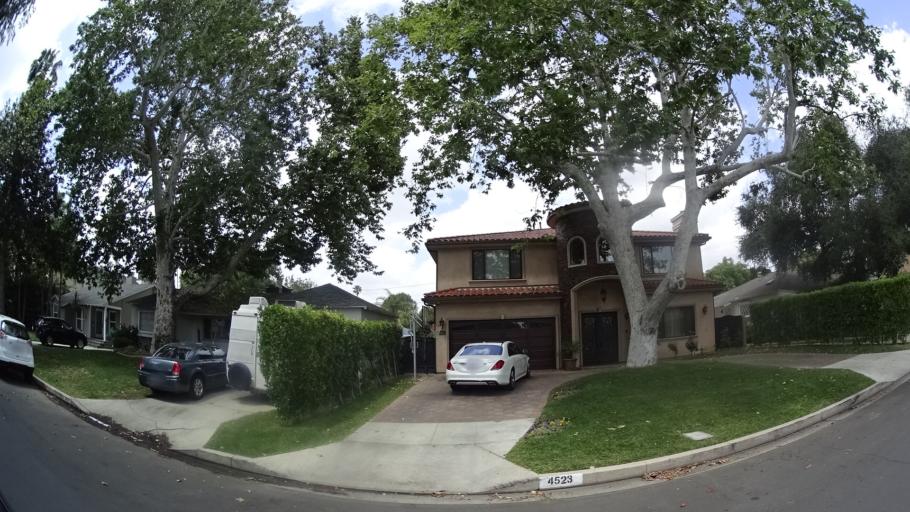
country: US
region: California
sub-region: Los Angeles County
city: Sherman Oaks
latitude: 34.1528
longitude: -118.4182
